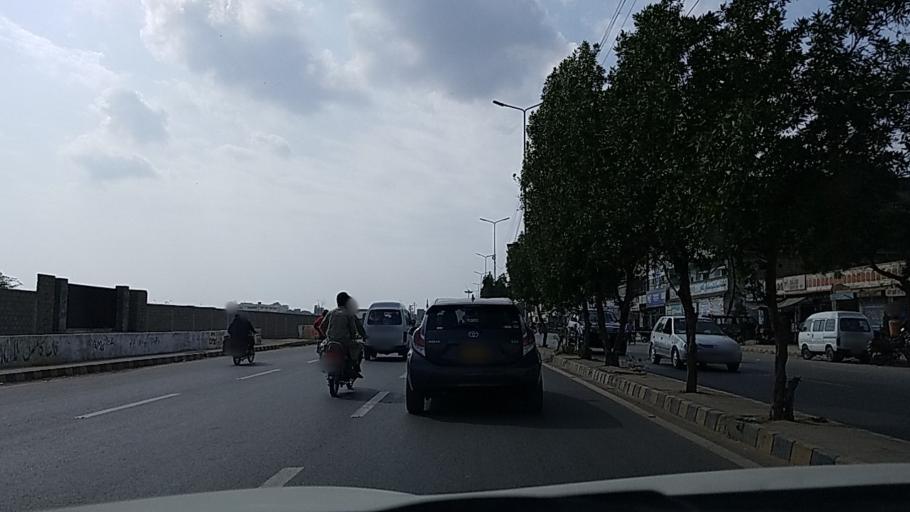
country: PK
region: Sindh
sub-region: Karachi District
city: Karachi
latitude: 24.8211
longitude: 67.1281
